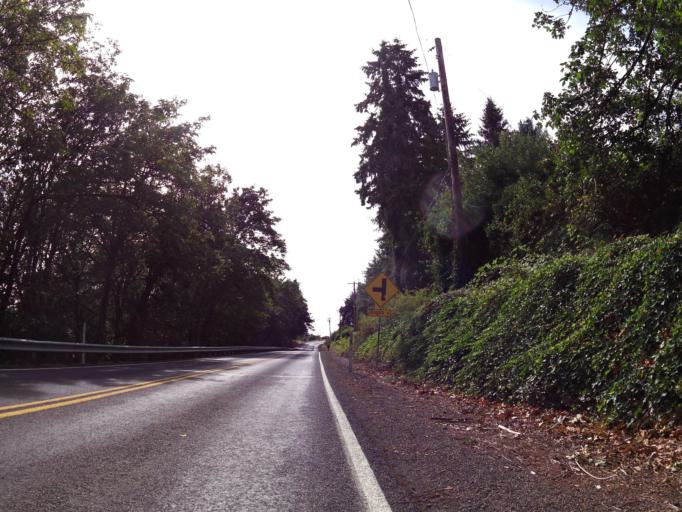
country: US
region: Washington
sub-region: Lewis County
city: Chehalis
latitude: 46.6293
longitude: -122.9683
